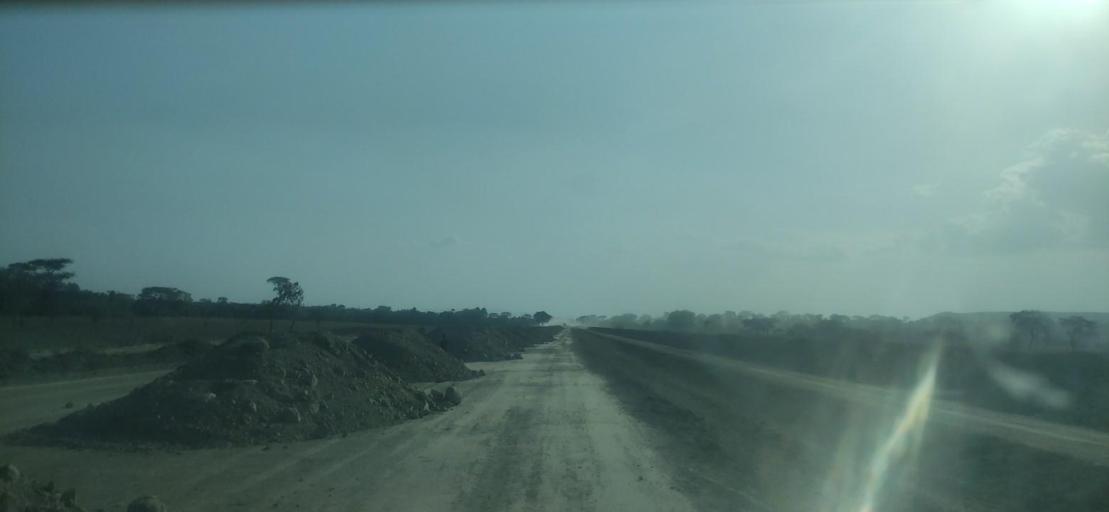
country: ET
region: Southern Nations, Nationalities, and People's Region
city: Hawassa
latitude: 7.1634
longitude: 38.4846
